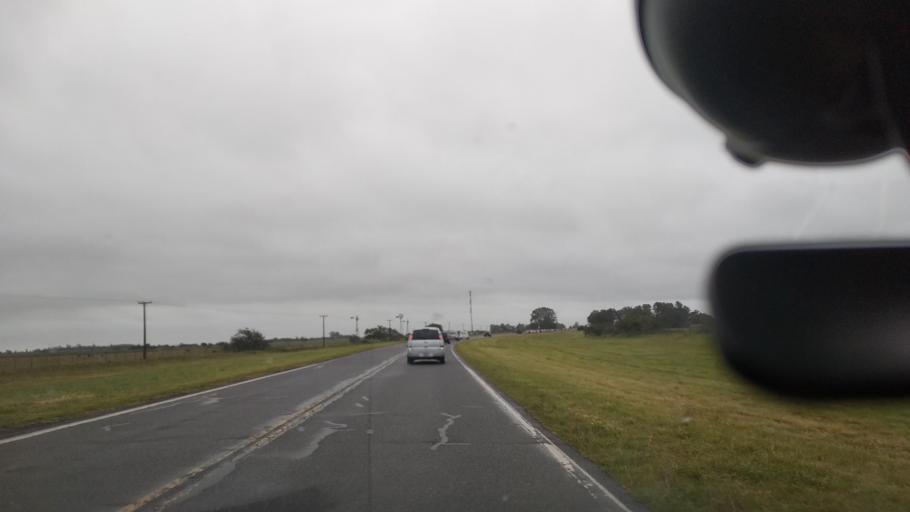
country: AR
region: Buenos Aires
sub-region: Partido de Castelli
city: Castelli
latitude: -35.9912
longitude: -57.4498
